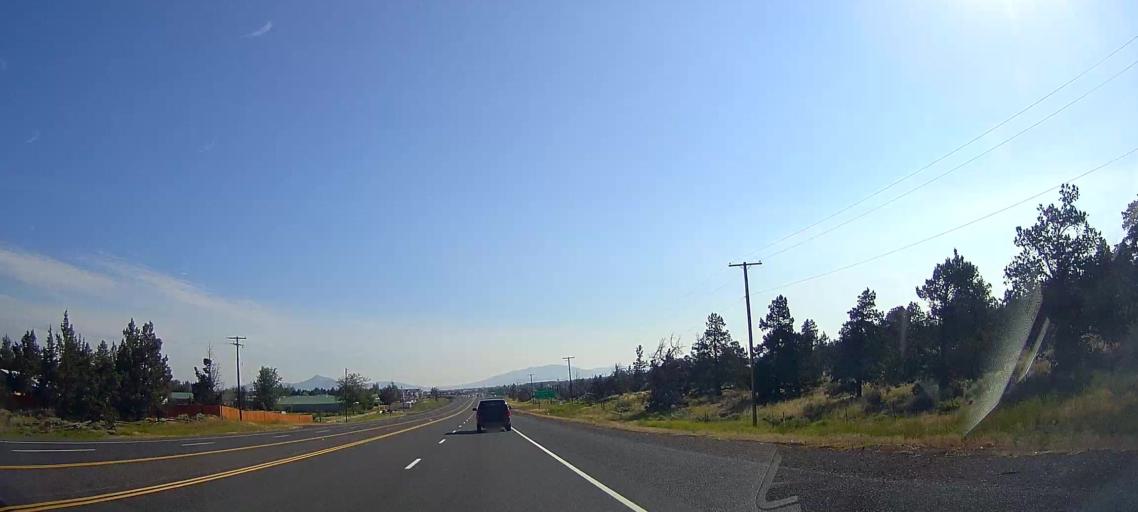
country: US
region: Oregon
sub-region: Deschutes County
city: Redmond
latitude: 44.2362
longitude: -121.1993
